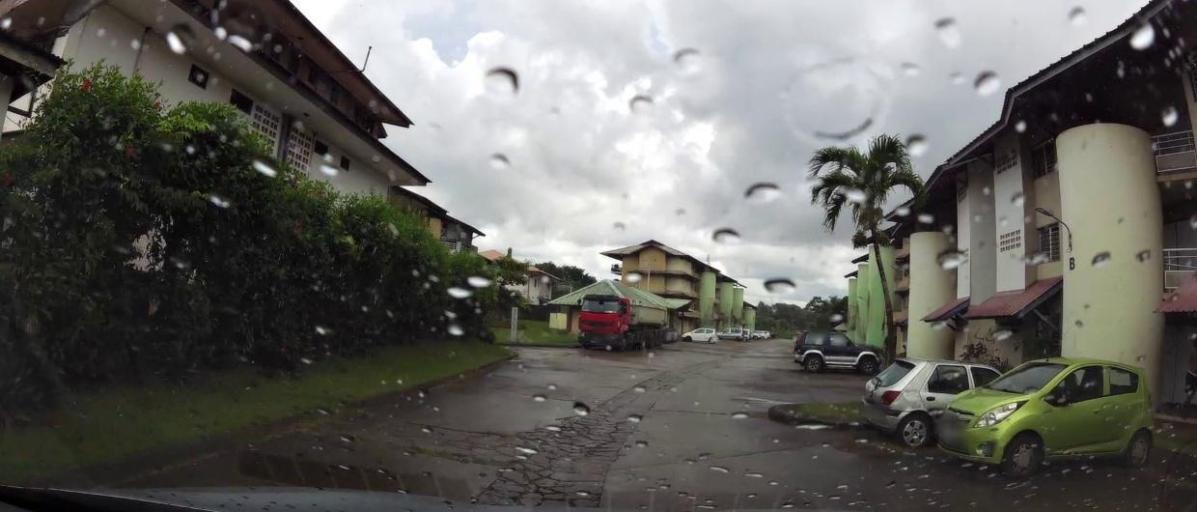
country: GF
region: Guyane
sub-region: Guyane
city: Cayenne
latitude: 4.9115
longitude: -52.3223
